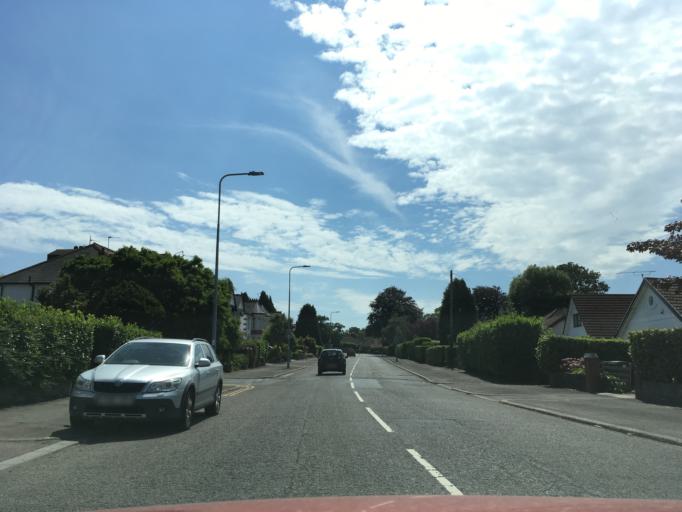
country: GB
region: Wales
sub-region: Cardiff
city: Cardiff
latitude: 51.5243
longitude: -3.1651
